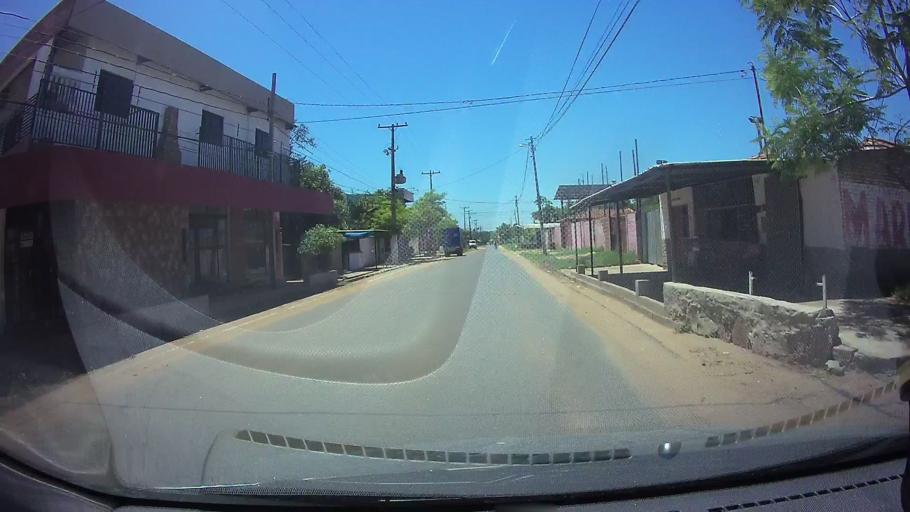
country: PY
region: Central
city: San Lorenzo
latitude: -25.3211
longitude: -57.4867
